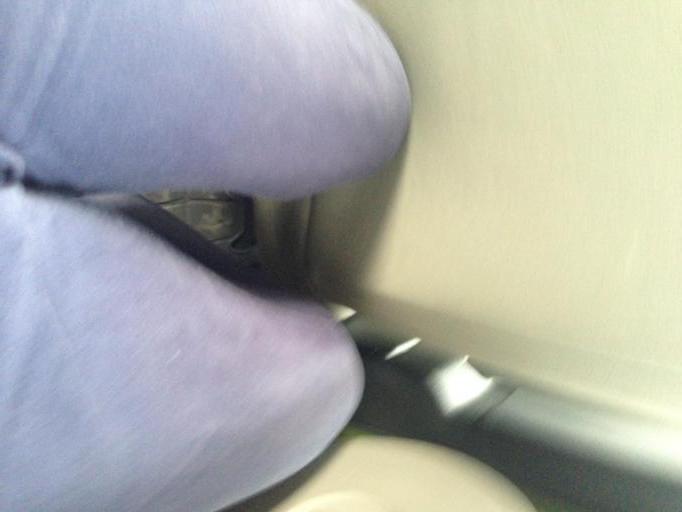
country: MX
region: Baja California
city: Tijuana
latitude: 32.5646
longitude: -116.9980
